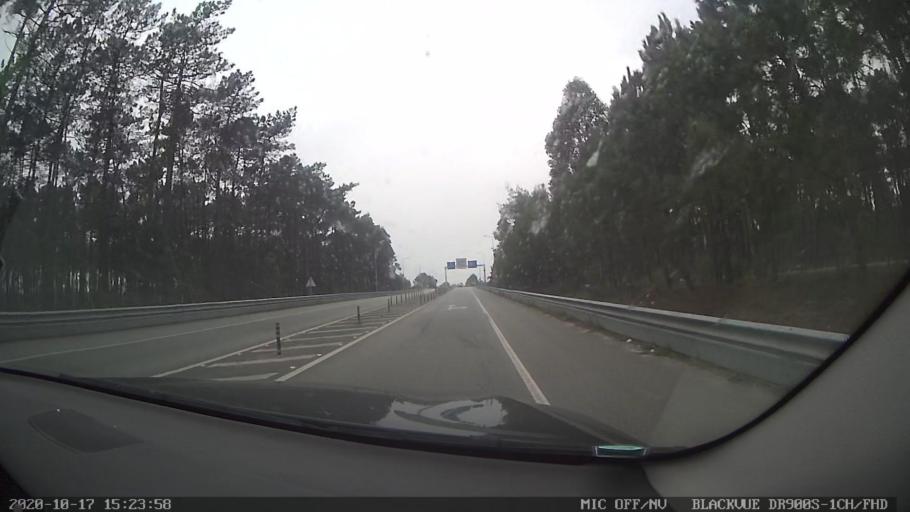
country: PT
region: Braga
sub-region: Esposende
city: Esposende
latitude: 41.5290
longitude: -8.7475
